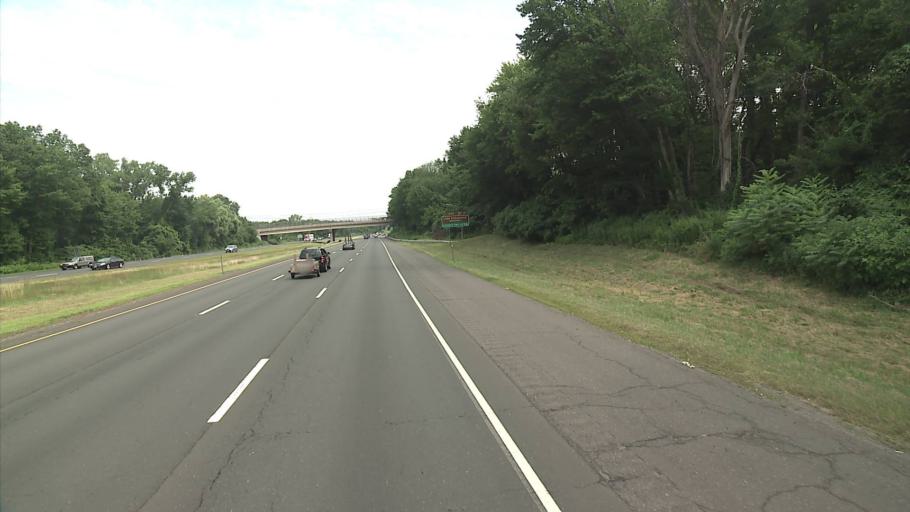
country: US
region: Connecticut
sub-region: Hartford County
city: Bristol
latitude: 41.6044
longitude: -72.9017
